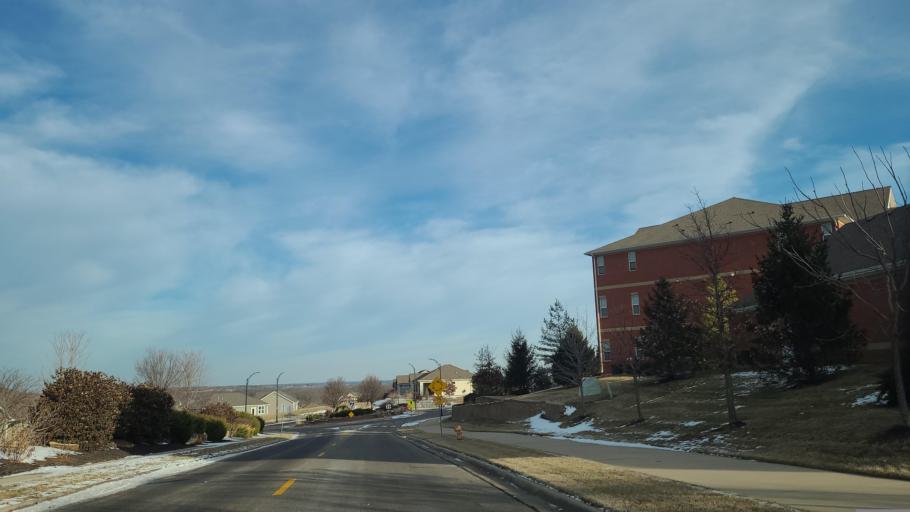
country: US
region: Kansas
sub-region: Douglas County
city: Lawrence
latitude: 38.9741
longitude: -95.3209
